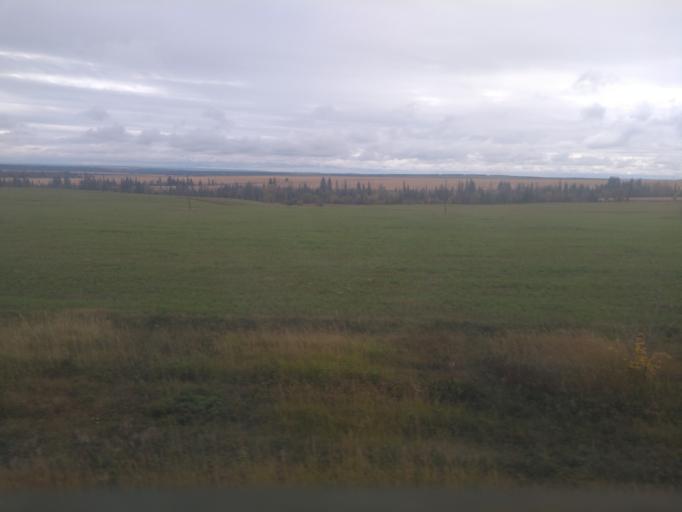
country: RU
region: Udmurtiya
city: Alnashi
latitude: 56.2162
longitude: 52.6332
